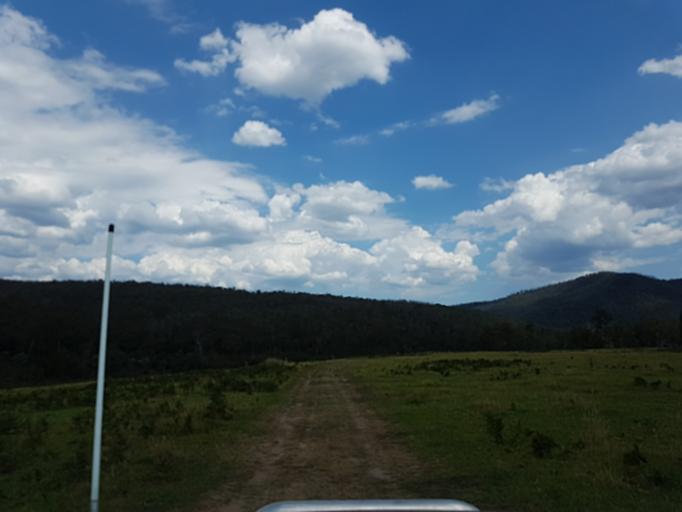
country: AU
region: Victoria
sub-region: East Gippsland
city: Lakes Entrance
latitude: -37.3980
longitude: 148.3340
